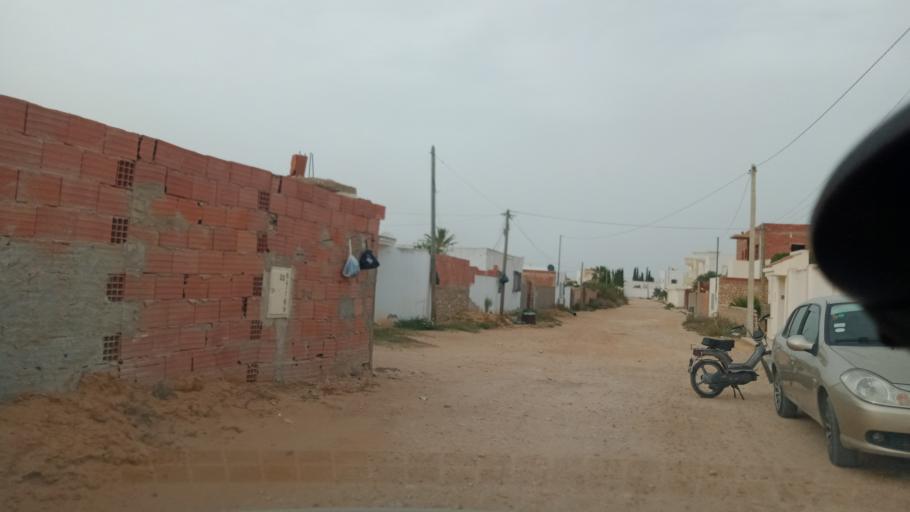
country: TN
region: Safaqis
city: Al Qarmadah
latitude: 34.7895
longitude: 10.7641
